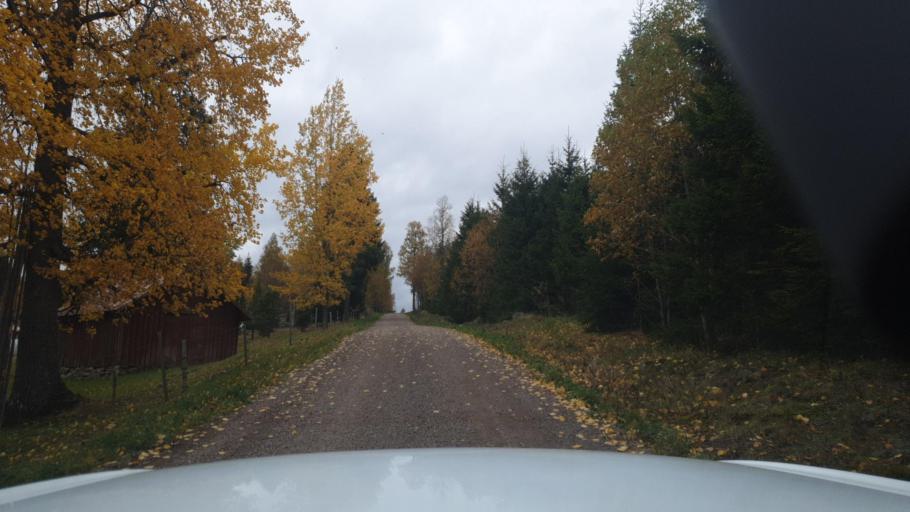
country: SE
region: Vaermland
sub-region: Torsby Kommun
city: Torsby
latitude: 59.9449
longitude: 12.7976
